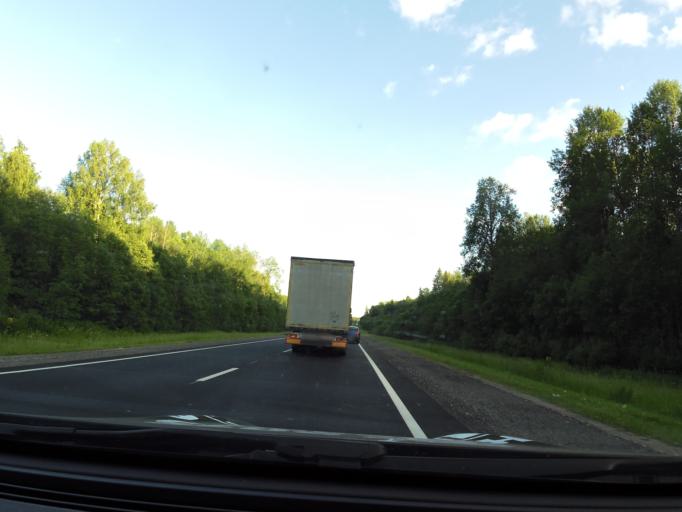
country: RU
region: Vologda
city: Gryazovets
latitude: 58.9430
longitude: 40.1739
